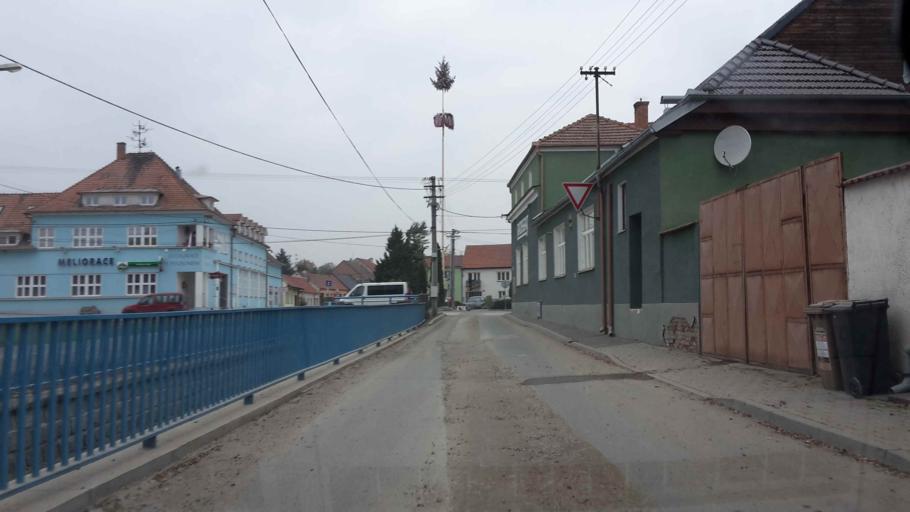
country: CZ
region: South Moravian
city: Damborice
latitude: 49.0401
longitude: 16.9672
